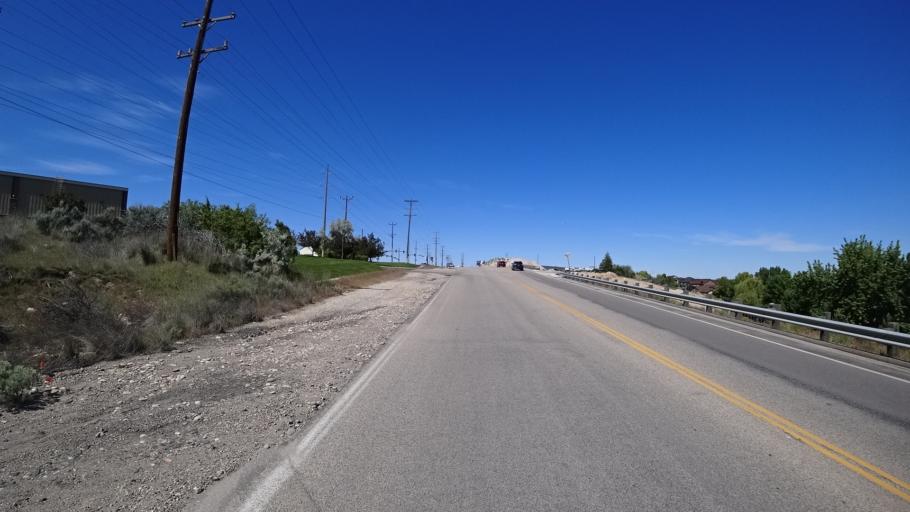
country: US
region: Idaho
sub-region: Ada County
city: Boise
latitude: 43.5608
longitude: -116.1660
